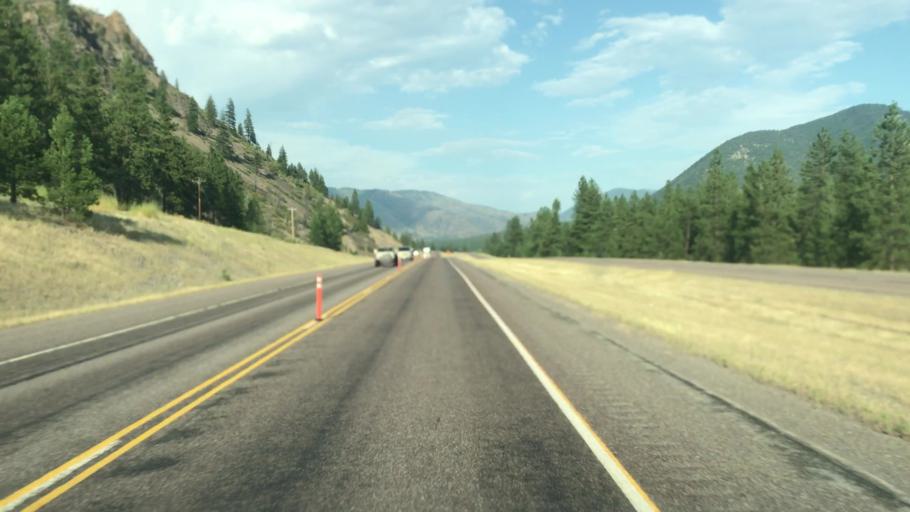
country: US
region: Montana
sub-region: Mineral County
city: Superior
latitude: 47.0123
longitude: -114.7104
